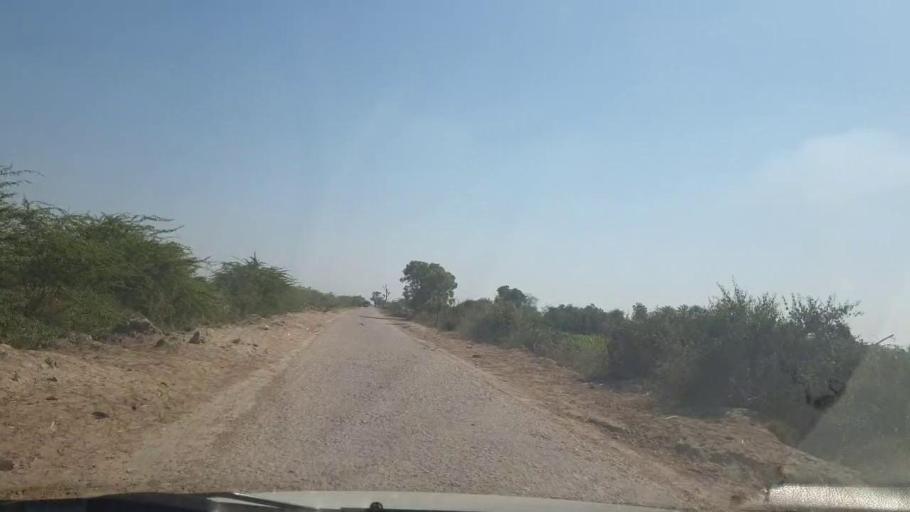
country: PK
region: Sindh
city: Mirpur Khas
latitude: 25.4878
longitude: 69.1687
